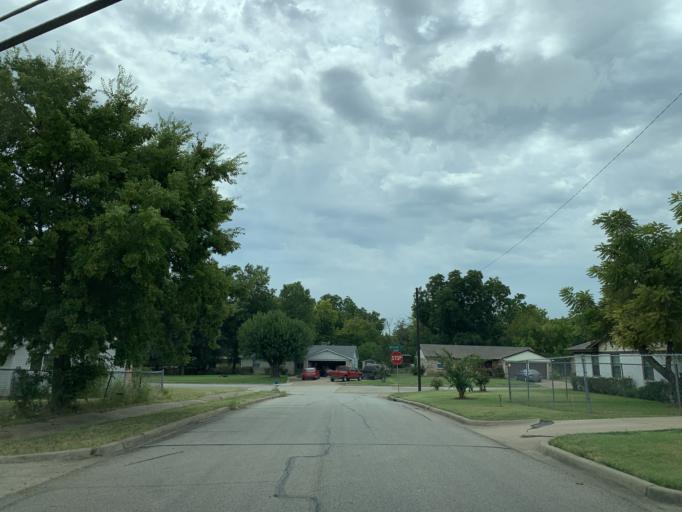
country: US
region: Texas
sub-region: Dallas County
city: DeSoto
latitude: 32.6544
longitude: -96.8319
